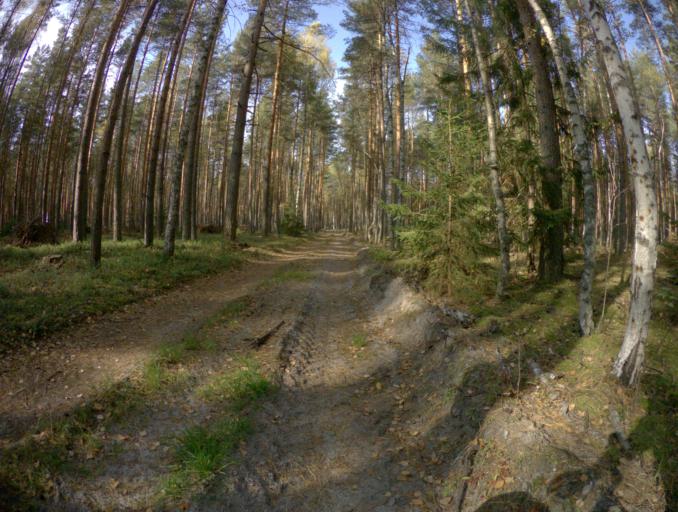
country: RU
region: Vladimir
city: Vorsha
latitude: 55.9385
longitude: 40.1279
